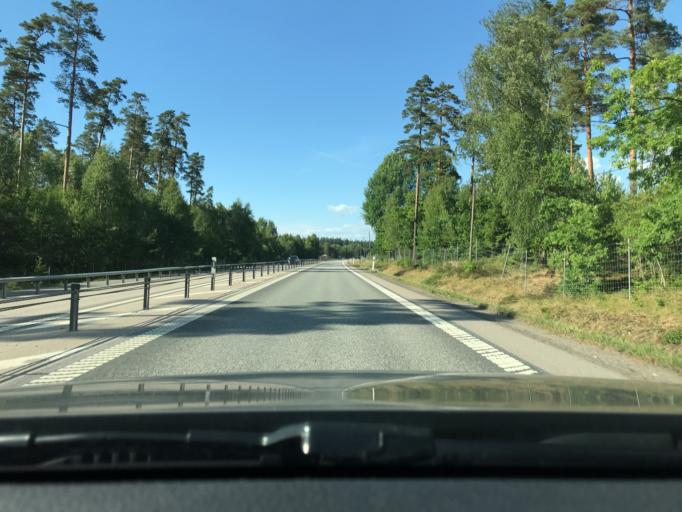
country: SE
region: Skane
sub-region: Osby Kommun
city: Osby
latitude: 56.3979
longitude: 14.0377
